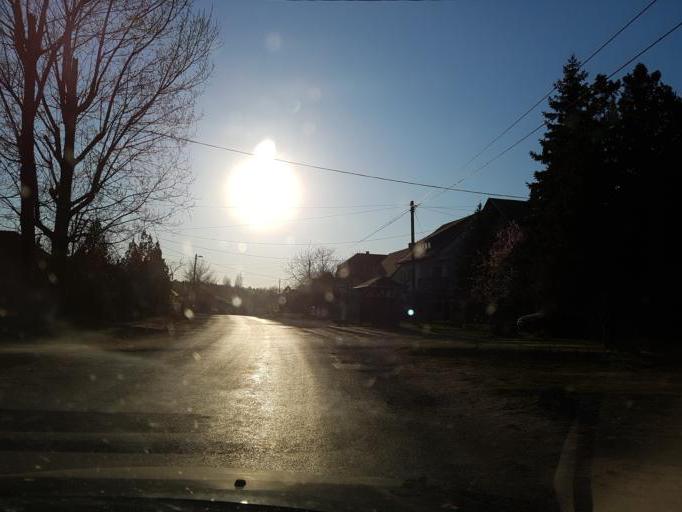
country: HU
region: Komarom-Esztergom
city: Piliscsev
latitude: 47.6727
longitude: 18.8074
